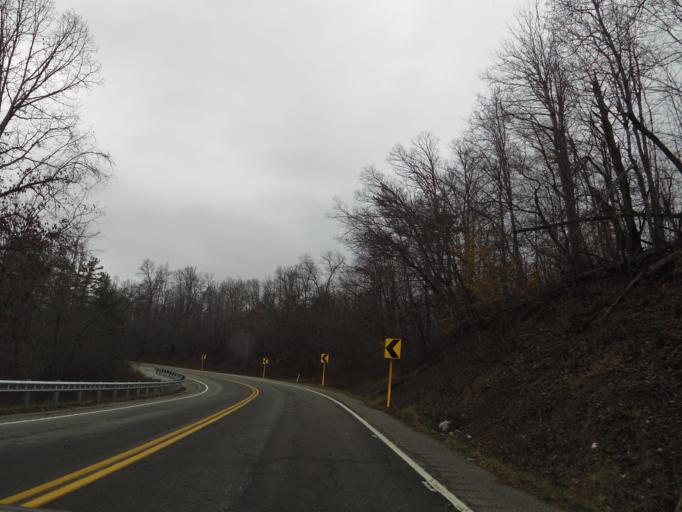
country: US
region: Tennessee
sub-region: Scott County
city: Huntsville
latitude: 36.3258
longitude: -84.6104
